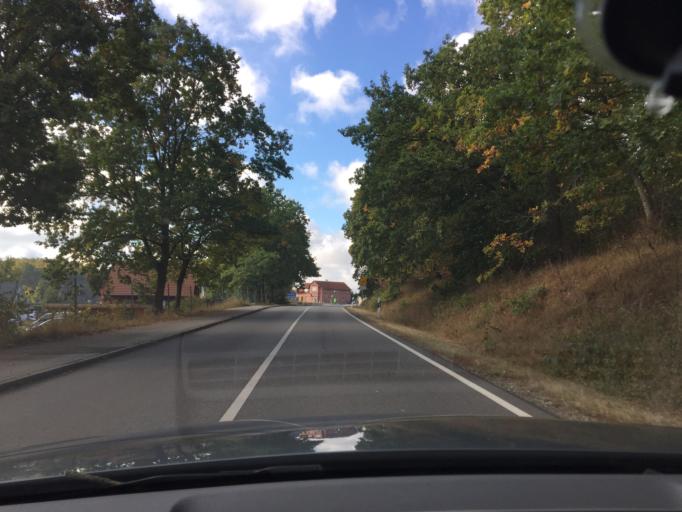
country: DE
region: Mecklenburg-Vorpommern
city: Krakow am See
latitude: 53.6692
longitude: 12.2704
